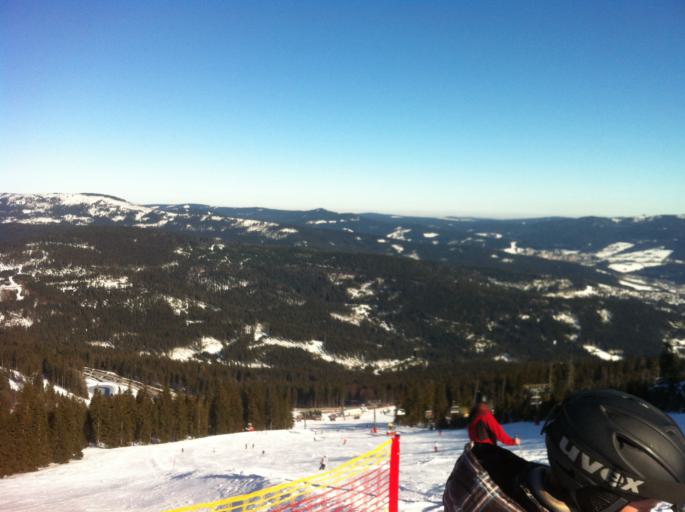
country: DE
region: Bavaria
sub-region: Lower Bavaria
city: Bodenmais
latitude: 49.1162
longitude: 13.1336
